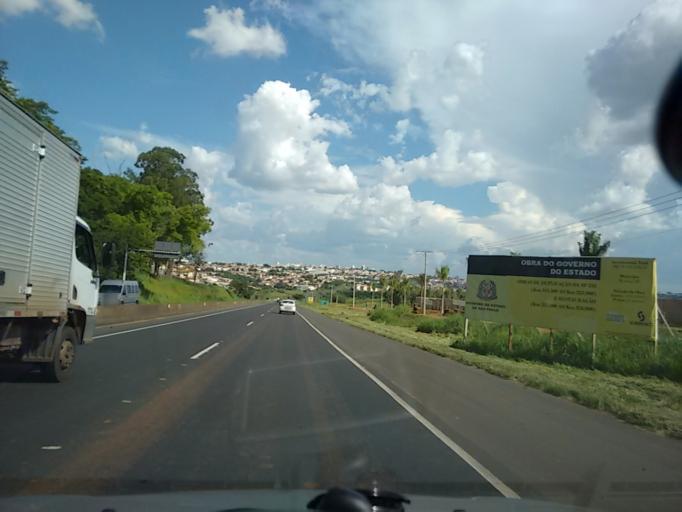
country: BR
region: Sao Paulo
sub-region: Marilia
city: Marilia
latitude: -22.1845
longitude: -49.9713
